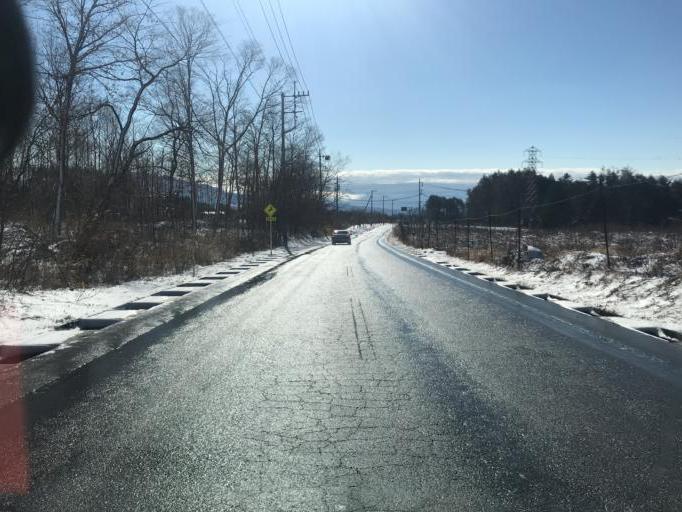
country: JP
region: Yamanashi
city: Nirasaki
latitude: 35.8656
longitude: 138.3360
